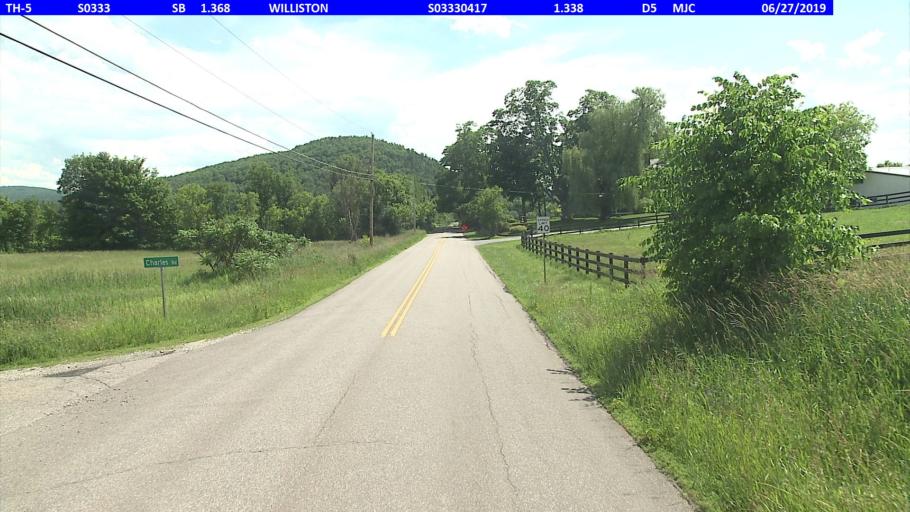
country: US
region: Vermont
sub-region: Chittenden County
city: South Burlington
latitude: 44.4204
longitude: -73.1360
